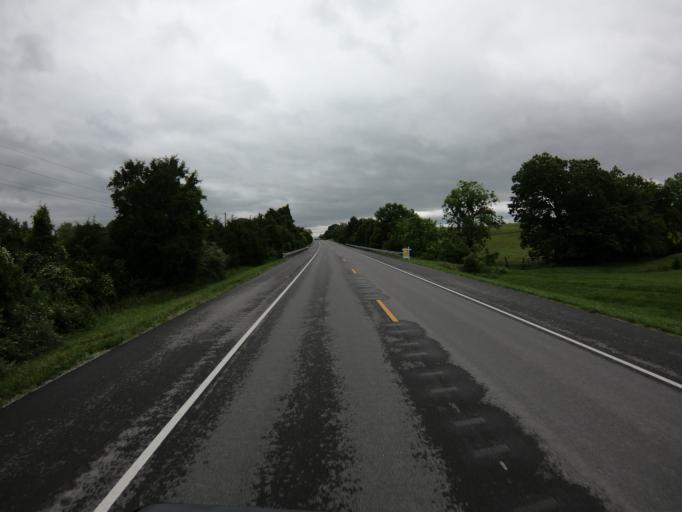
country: US
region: Maryland
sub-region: Washington County
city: Keedysville
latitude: 39.4711
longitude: -77.7136
